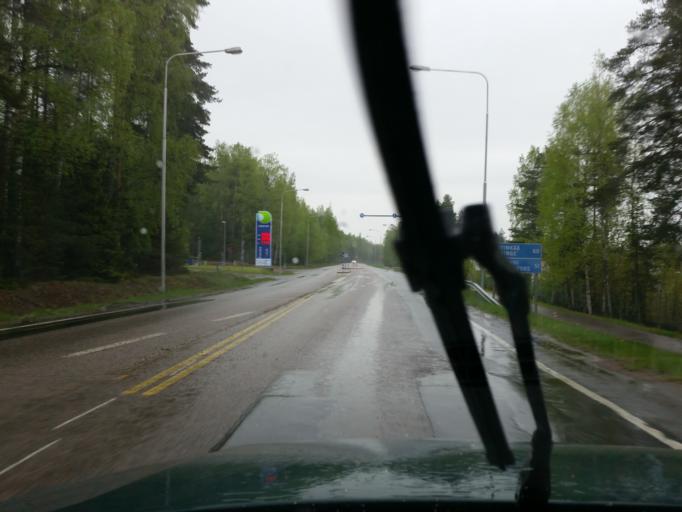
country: FI
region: Uusimaa
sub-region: Helsinki
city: Lohja
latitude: 60.2811
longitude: 24.1578
